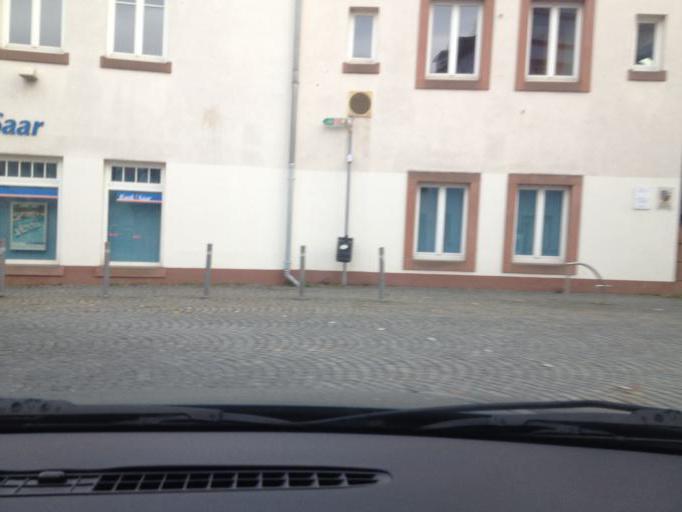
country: DE
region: Saarland
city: Ottweiler
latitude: 49.4040
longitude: 7.1613
